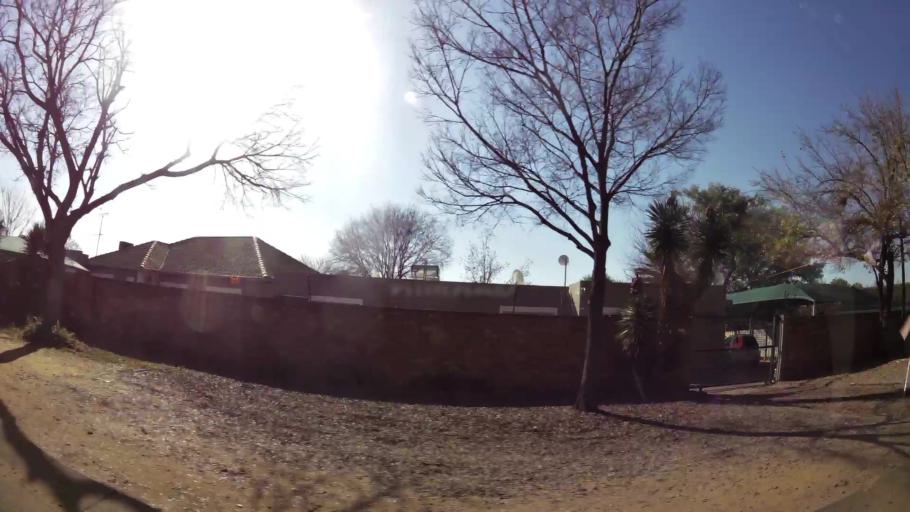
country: ZA
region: Gauteng
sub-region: City of Tshwane Metropolitan Municipality
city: Pretoria
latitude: -25.7233
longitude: 28.2427
